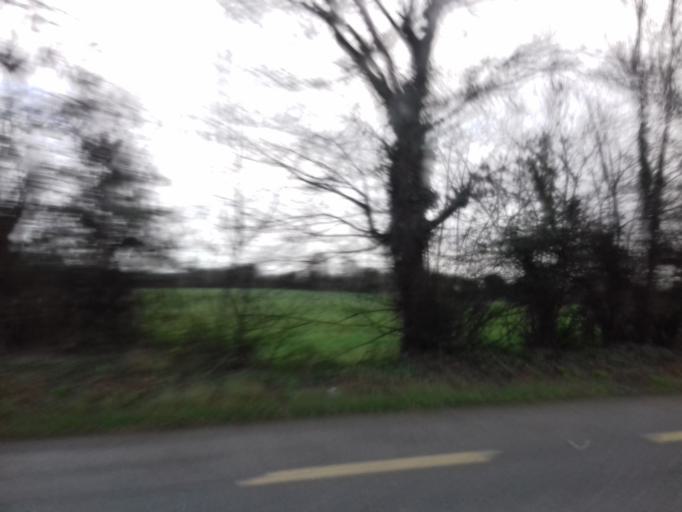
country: IE
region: Leinster
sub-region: An Mhi
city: Ashbourne
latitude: 53.5343
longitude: -6.4226
